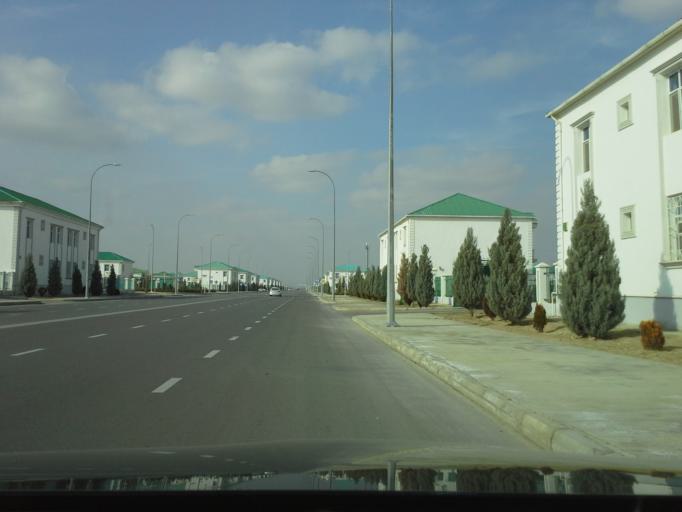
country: TM
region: Ahal
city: Abadan
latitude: 38.0804
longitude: 58.2747
